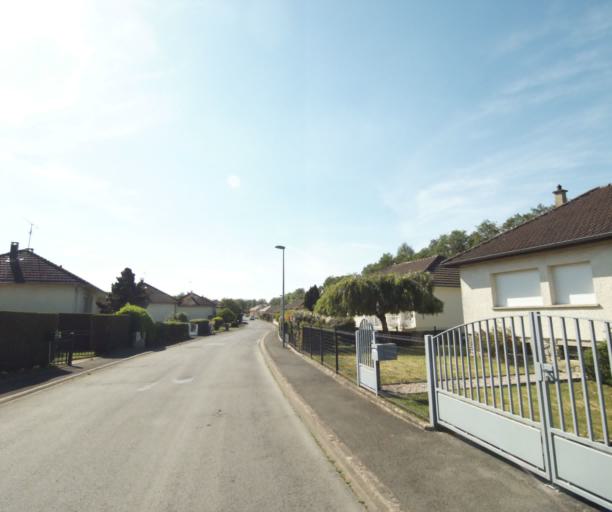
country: FR
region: Champagne-Ardenne
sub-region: Departement des Ardennes
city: Warcq
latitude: 49.7818
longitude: 4.6985
